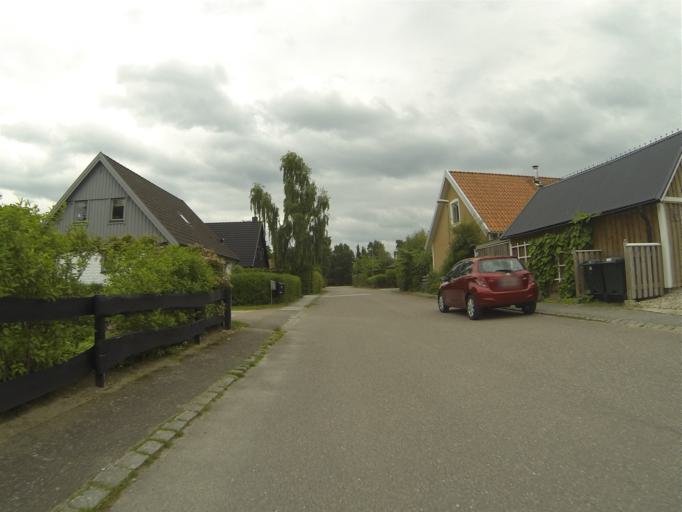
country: SE
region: Skane
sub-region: Lunds Kommun
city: Genarp
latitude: 55.7169
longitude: 13.3551
